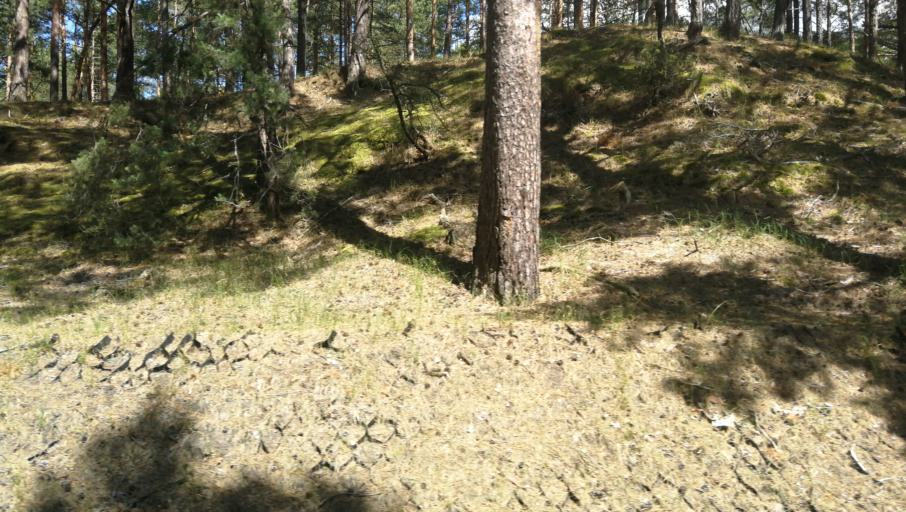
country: PL
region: Pomeranian Voivodeship
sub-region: Powiat pucki
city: Hel
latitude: 54.6302
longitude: 18.8027
